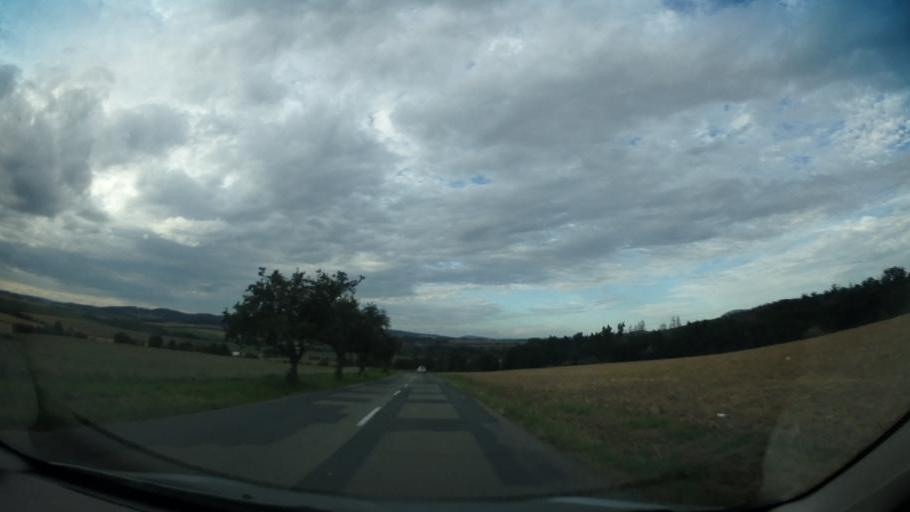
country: CZ
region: South Moravian
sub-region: Okres Blansko
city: Boskovice
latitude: 49.5038
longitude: 16.6693
